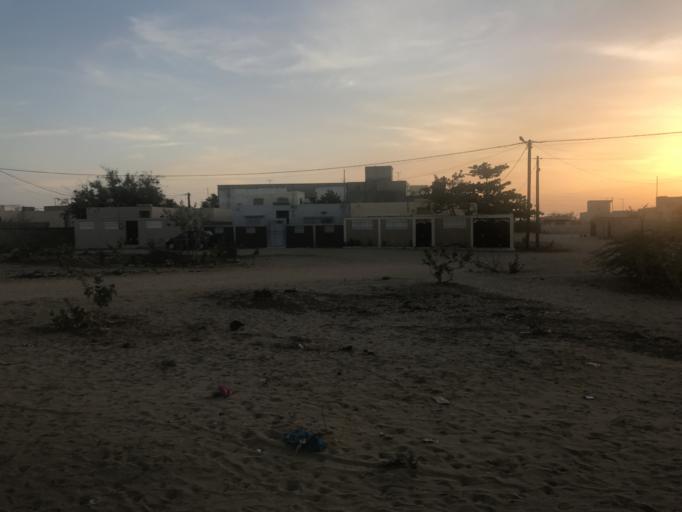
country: SN
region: Saint-Louis
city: Saint-Louis
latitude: 16.0508
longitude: -16.4338
